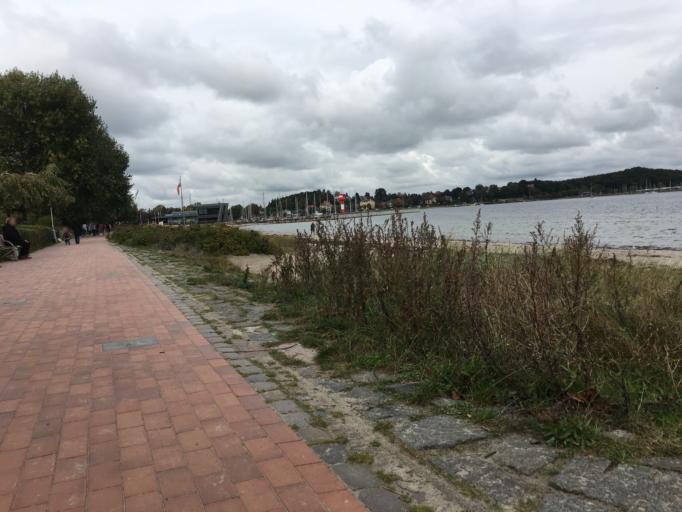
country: DE
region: Schleswig-Holstein
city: Eckernforde
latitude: 54.4708
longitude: 9.8402
